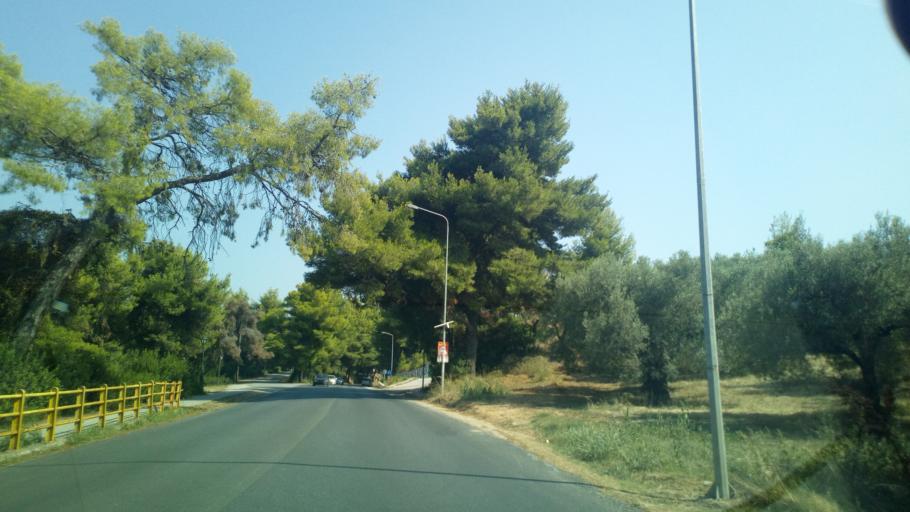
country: GR
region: Central Macedonia
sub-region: Nomos Chalkidikis
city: Kallithea
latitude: 40.0710
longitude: 23.4509
